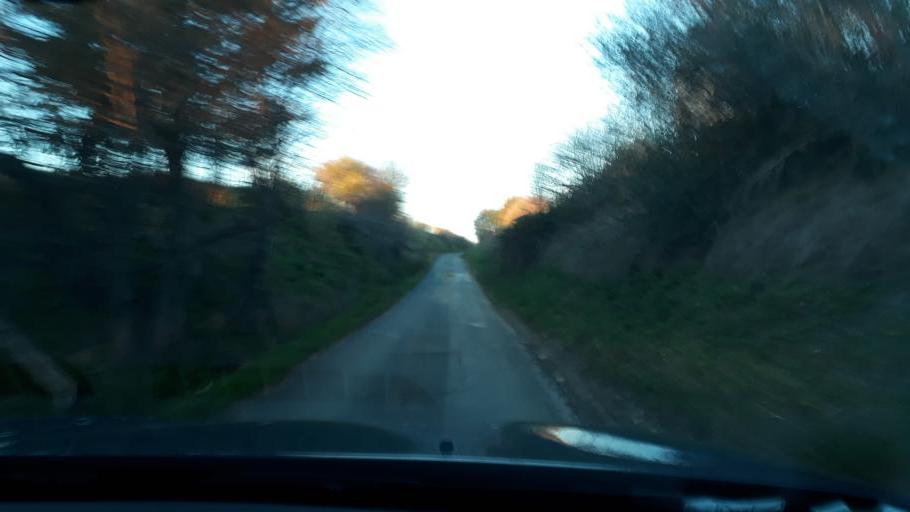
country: FR
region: Languedoc-Roussillon
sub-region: Departement de l'Herault
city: Florensac
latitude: 43.3968
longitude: 3.4593
